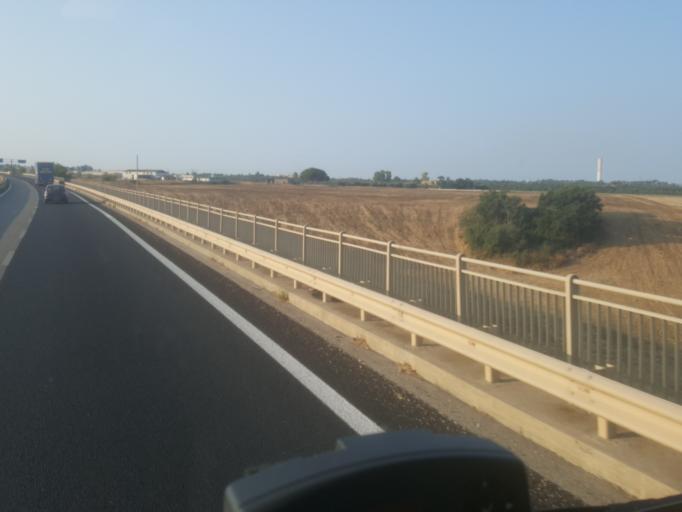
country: IT
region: Latium
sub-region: Citta metropolitana di Roma Capitale
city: Aurelia
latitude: 42.1603
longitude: 11.7887
